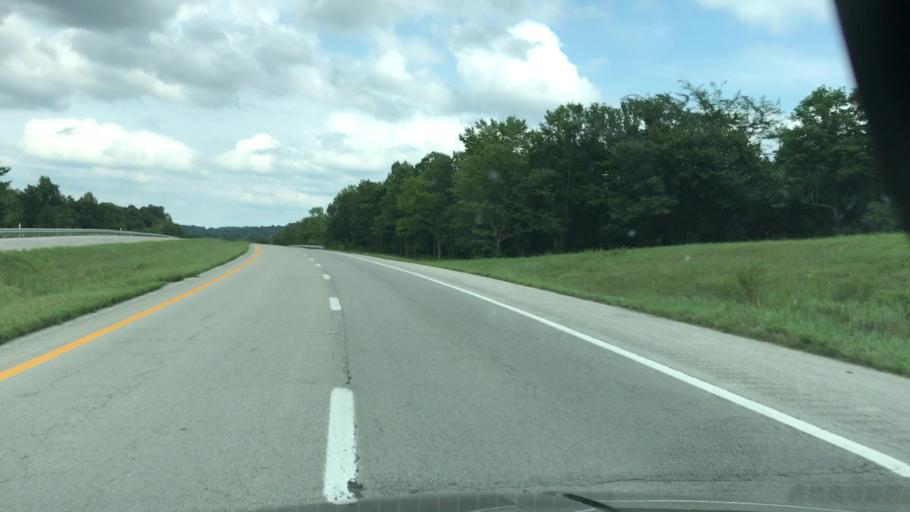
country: US
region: Kentucky
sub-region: Caldwell County
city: Princeton
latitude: 37.1403
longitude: -87.8147
